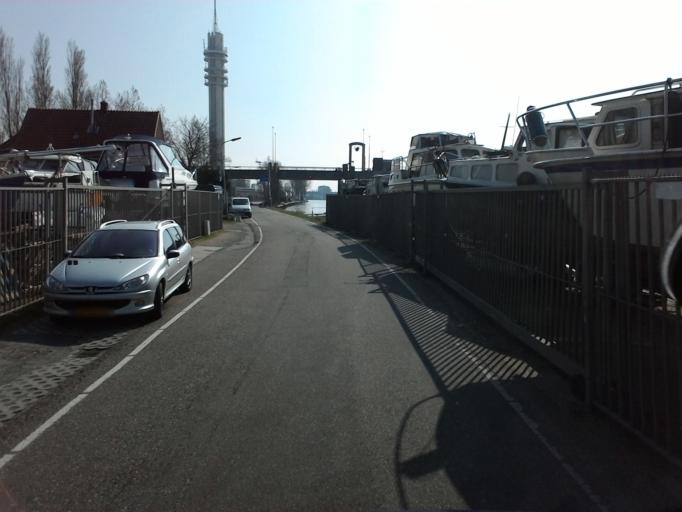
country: NL
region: North Holland
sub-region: Gemeente Zaanstad
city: Zaanstad
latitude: 52.5017
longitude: 4.7952
